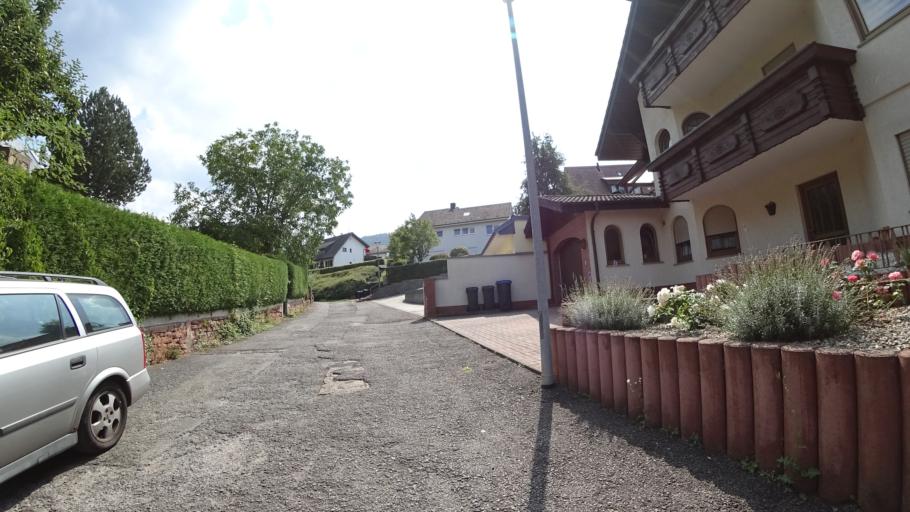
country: DE
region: Bavaria
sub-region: Regierungsbezirk Unterfranken
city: Miltenberg
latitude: 49.7016
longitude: 9.2650
